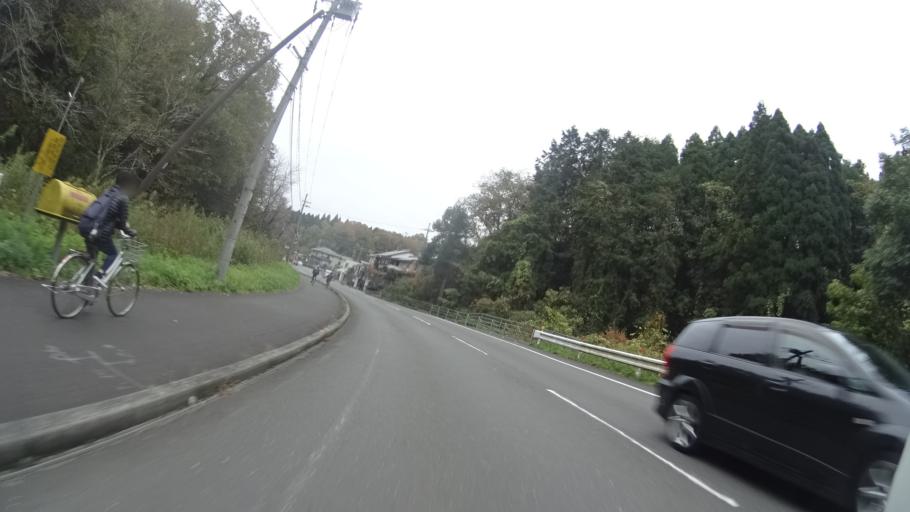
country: JP
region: Kyoto
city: Maizuru
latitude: 35.4933
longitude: 135.4370
